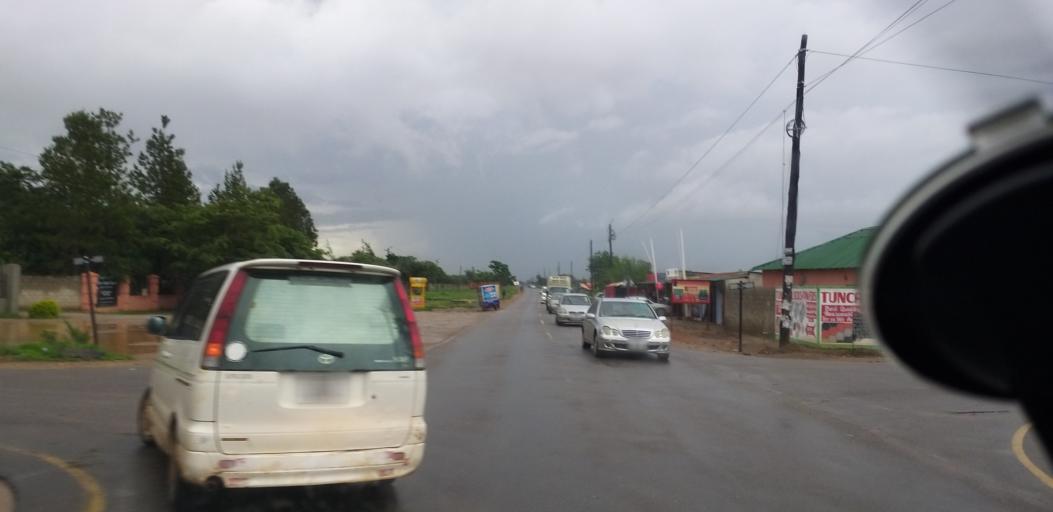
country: ZM
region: Lusaka
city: Lusaka
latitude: -15.4771
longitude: 28.3161
